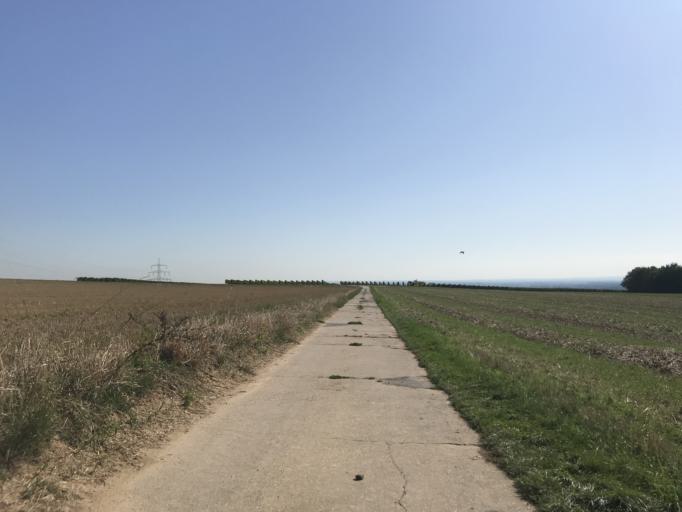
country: DE
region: Rheinland-Pfalz
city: Bodenheim
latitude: 49.9496
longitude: 8.2937
